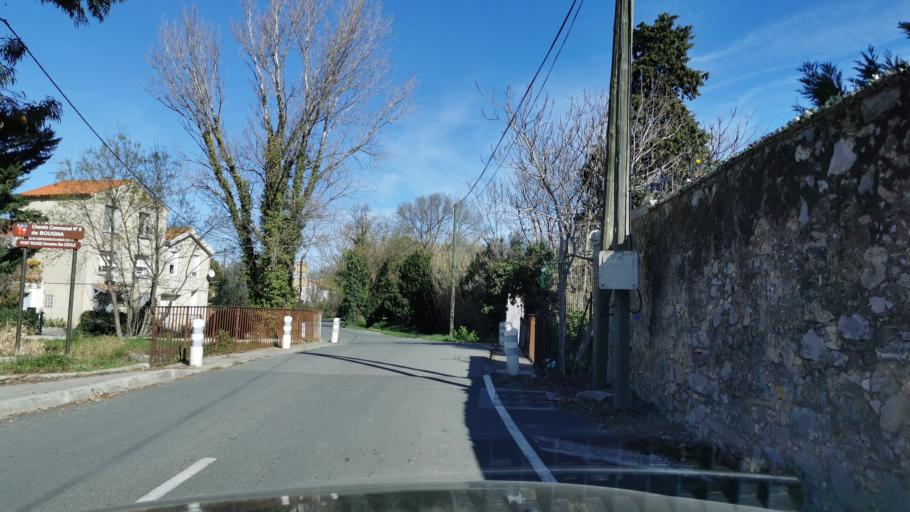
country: FR
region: Languedoc-Roussillon
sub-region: Departement de l'Aude
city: Narbonne
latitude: 43.1897
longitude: 2.9903
